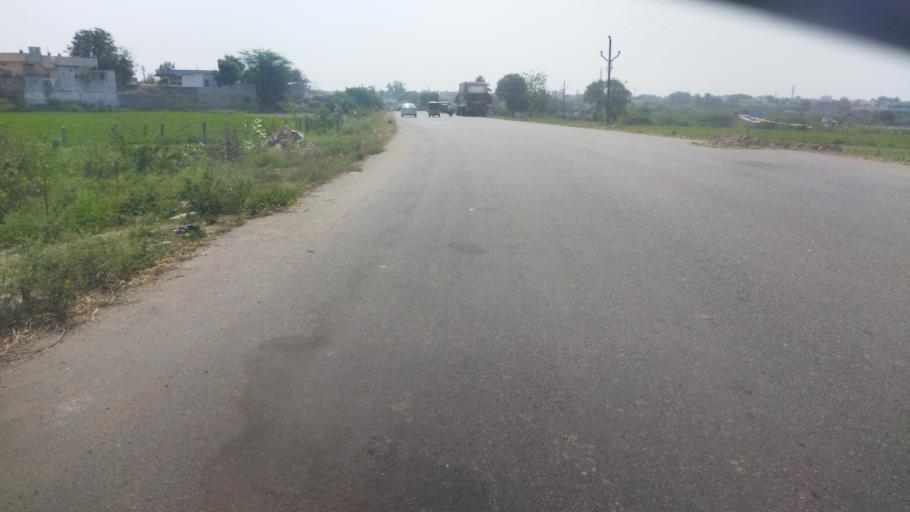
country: IN
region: Telangana
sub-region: Nalgonda
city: Nalgonda
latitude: 17.0780
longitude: 79.2835
